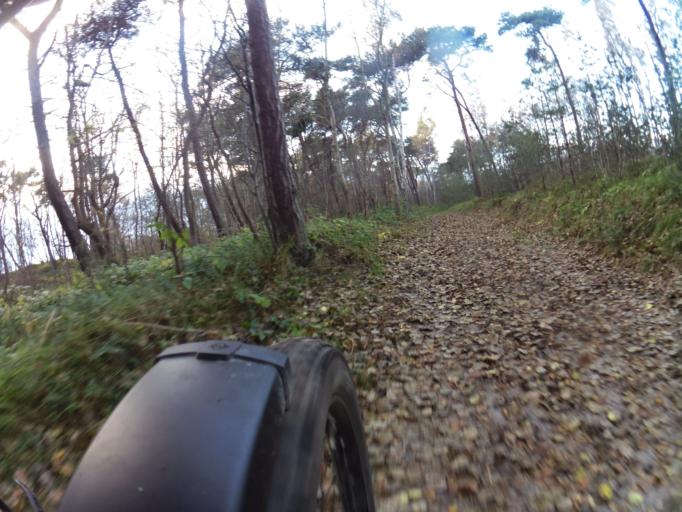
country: PL
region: Pomeranian Voivodeship
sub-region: Powiat pucki
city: Jastarnia
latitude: 54.7255
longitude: 18.6101
